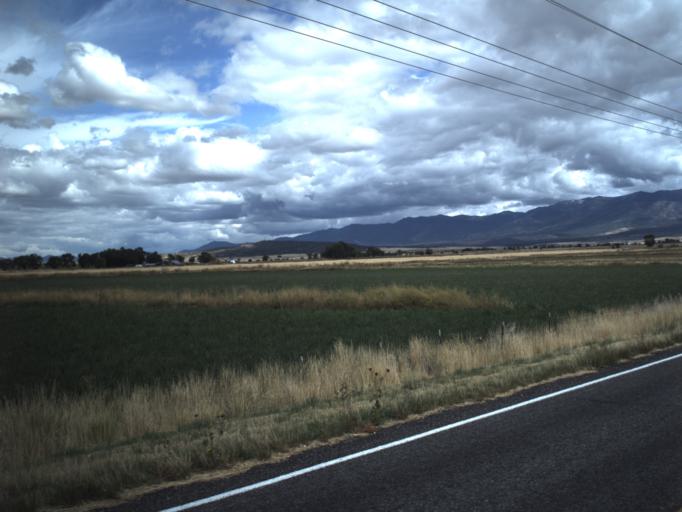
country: US
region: Utah
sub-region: Millard County
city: Fillmore
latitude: 38.9792
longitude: -112.4083
